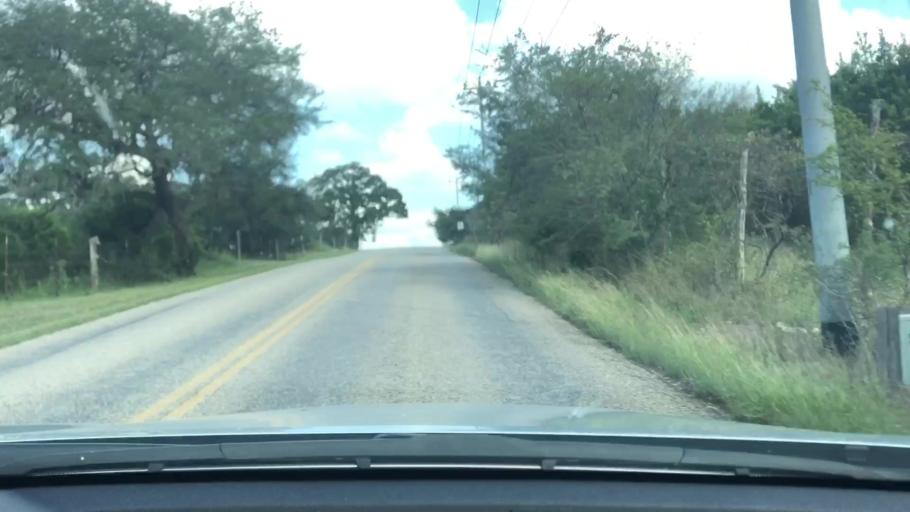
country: US
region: Texas
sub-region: Bexar County
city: Fair Oaks Ranch
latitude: 29.7851
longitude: -98.6312
